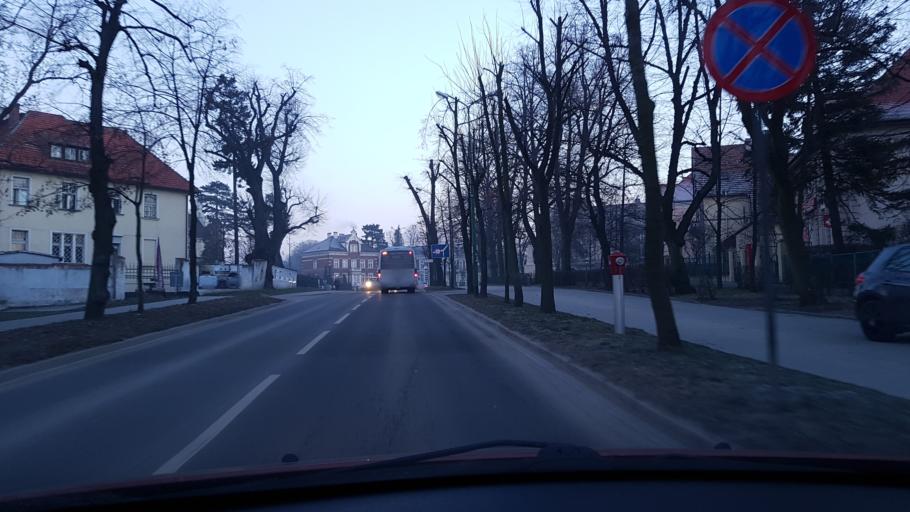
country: PL
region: Lower Silesian Voivodeship
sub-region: Powiat zabkowicki
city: Zabkowice Slaskie
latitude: 50.5955
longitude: 16.8111
